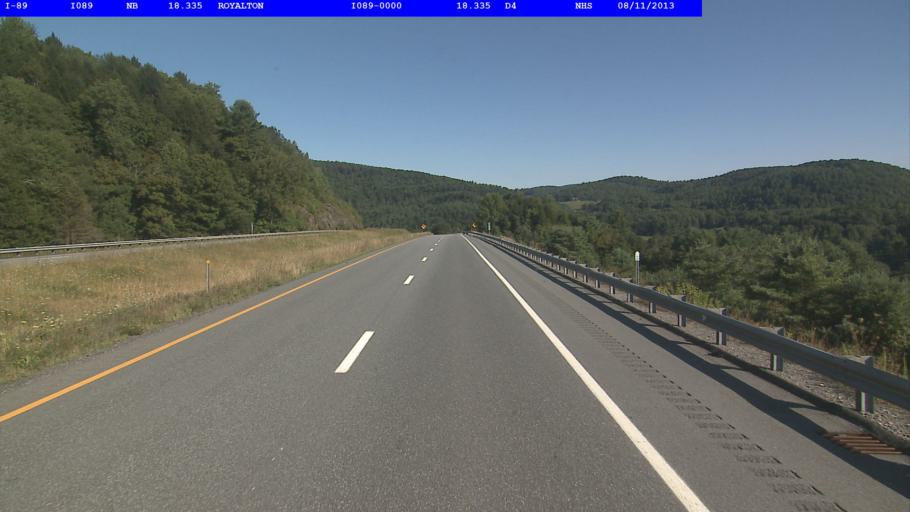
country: US
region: Vermont
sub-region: Orange County
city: Randolph
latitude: 43.8184
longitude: -72.5253
